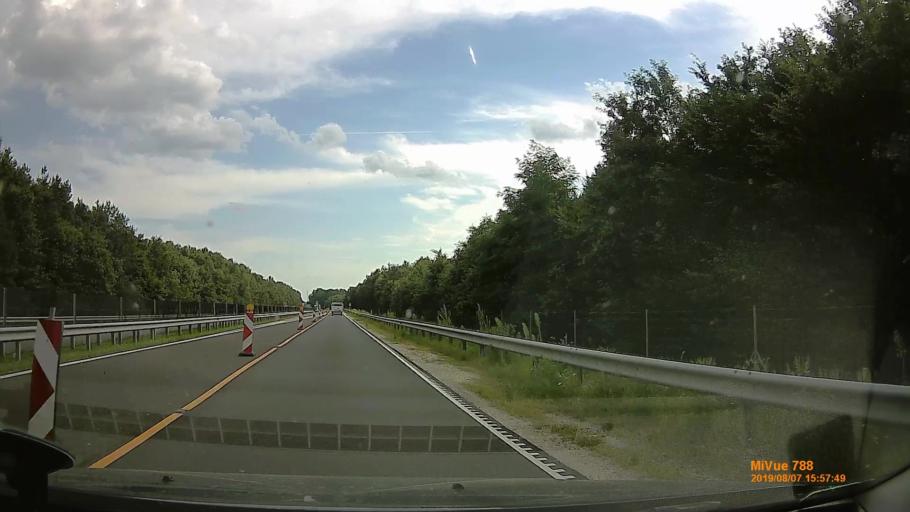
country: HU
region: Vas
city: Kormend
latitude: 47.0355
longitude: 16.6129
